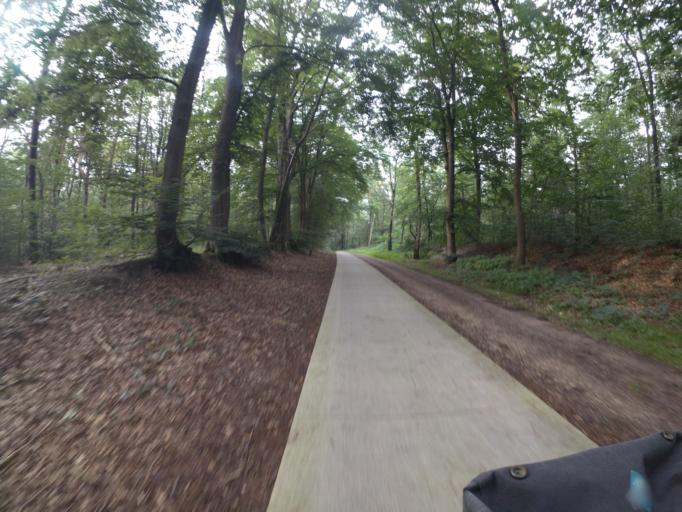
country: NL
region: Gelderland
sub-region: Gemeente Groesbeek
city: Groesbeek
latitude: 51.7713
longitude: 5.9008
